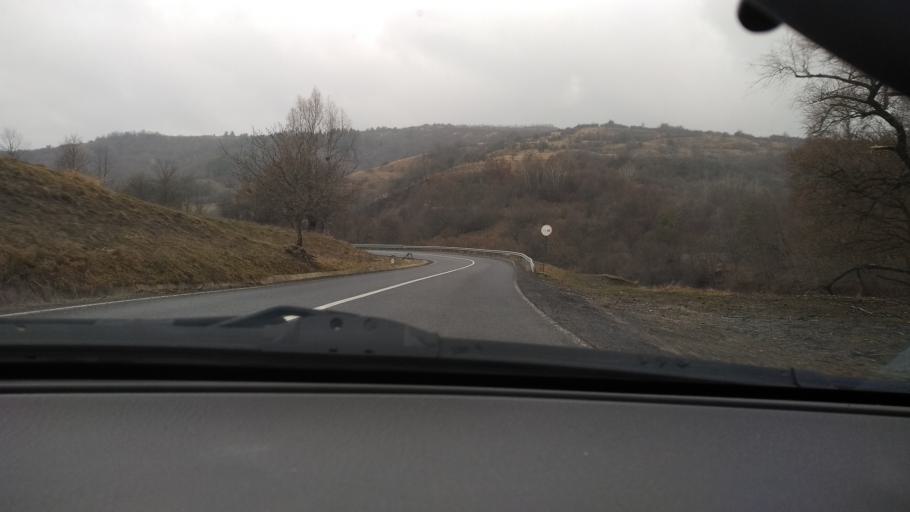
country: RO
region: Mures
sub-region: Comuna Magherani
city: Magherani
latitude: 46.5818
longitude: 24.9439
